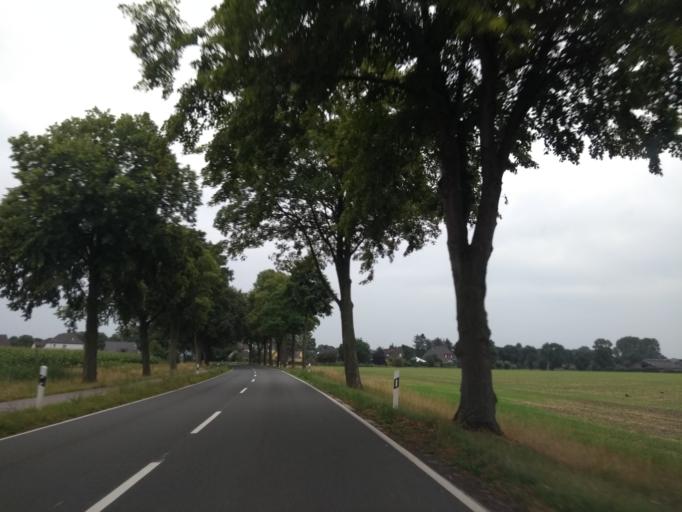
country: DE
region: North Rhine-Westphalia
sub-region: Regierungsbezirk Dusseldorf
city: Kleve
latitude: 51.8294
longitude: 6.1014
